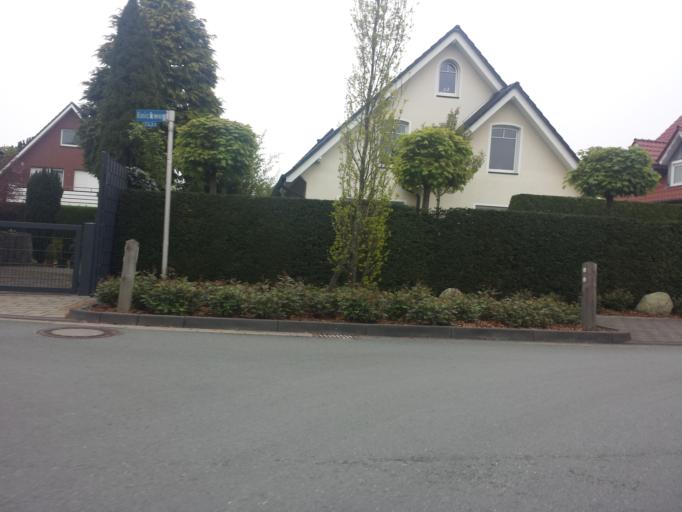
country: DE
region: North Rhine-Westphalia
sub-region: Regierungsbezirk Detmold
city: Guetersloh
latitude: 51.8912
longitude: 8.3773
